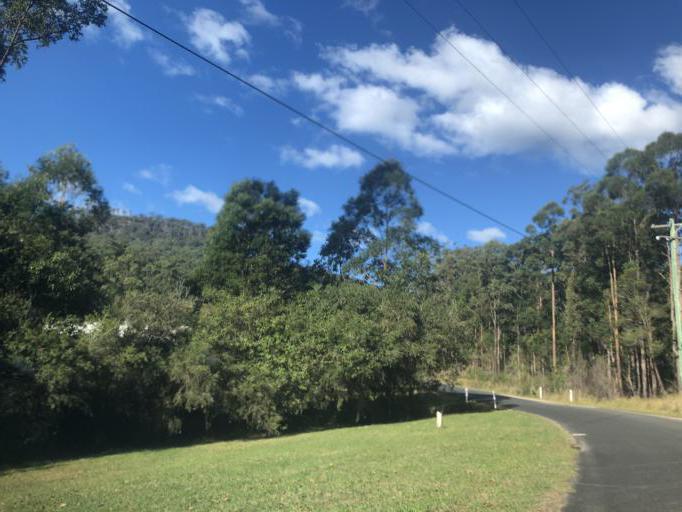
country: AU
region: New South Wales
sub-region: Coffs Harbour
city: Nana Glen
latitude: -30.0568
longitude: 152.9865
